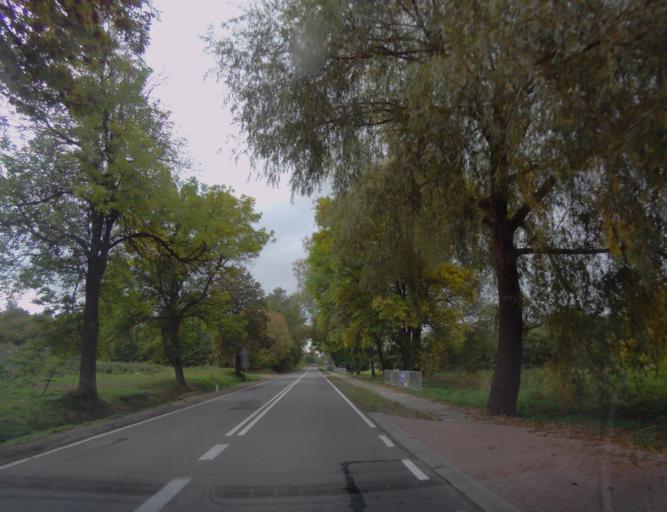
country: PL
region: Lublin Voivodeship
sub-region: Powiat krasnostawski
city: Rudnik
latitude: 50.9285
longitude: 22.9125
